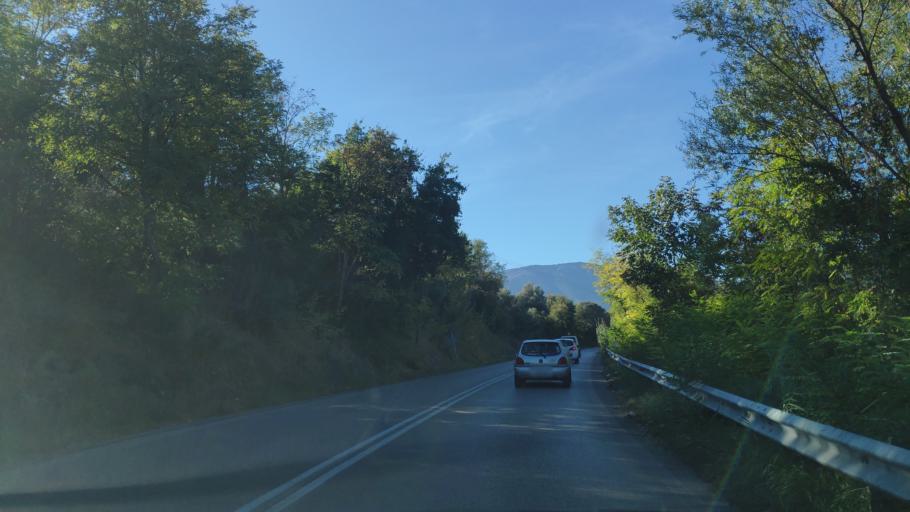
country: GR
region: Central Greece
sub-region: Nomos Voiotias
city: Livadeia
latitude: 38.4490
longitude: 22.8821
